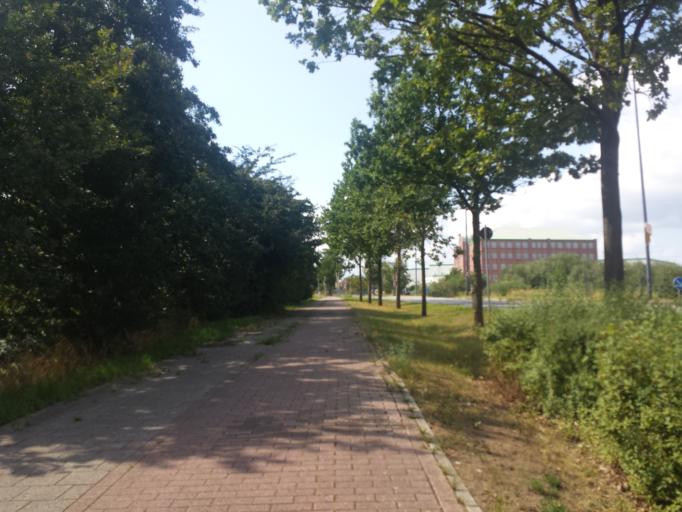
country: DE
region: Lower Saxony
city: Stuhr
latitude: 53.0886
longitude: 8.7193
